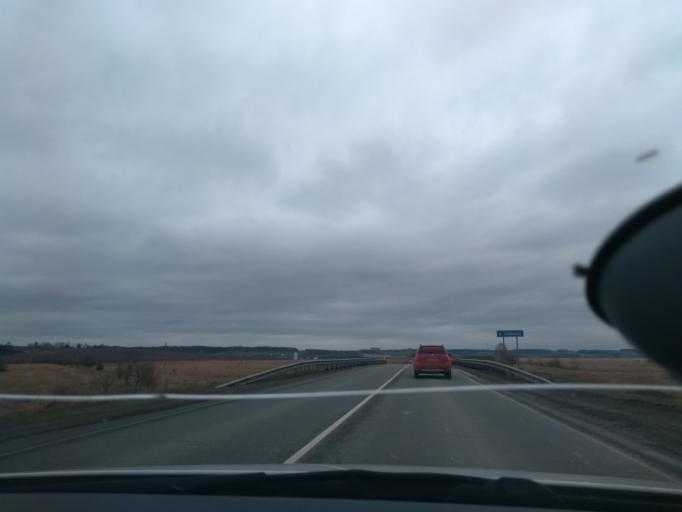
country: RU
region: Perm
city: Kukushtan
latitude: 57.4965
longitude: 56.6590
